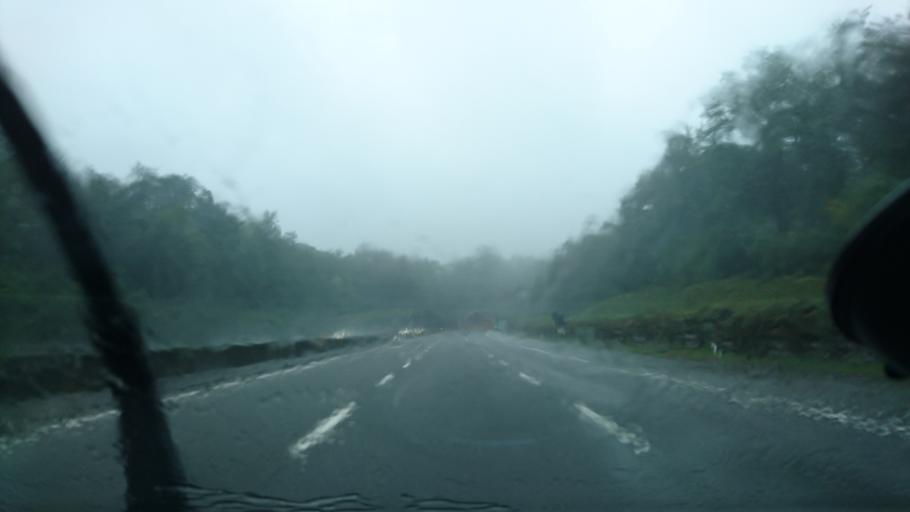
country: IT
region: Piedmont
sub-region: Provincia di Novara
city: Gattico
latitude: 45.7166
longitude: 8.5332
